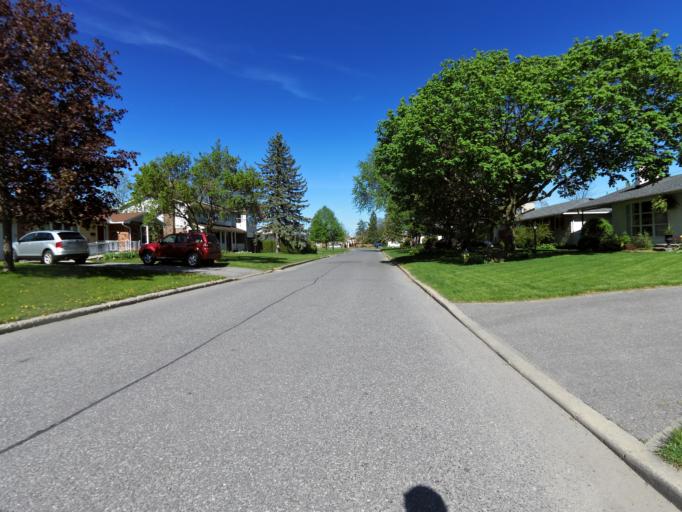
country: CA
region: Ontario
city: Bells Corners
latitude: 45.3315
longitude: -75.7637
